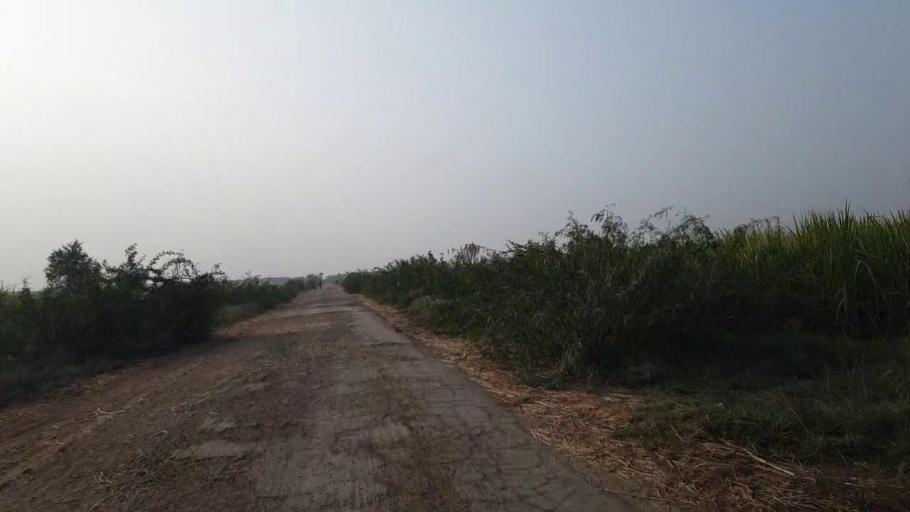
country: PK
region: Sindh
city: Tando Muhammad Khan
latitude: 25.1427
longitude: 68.6038
